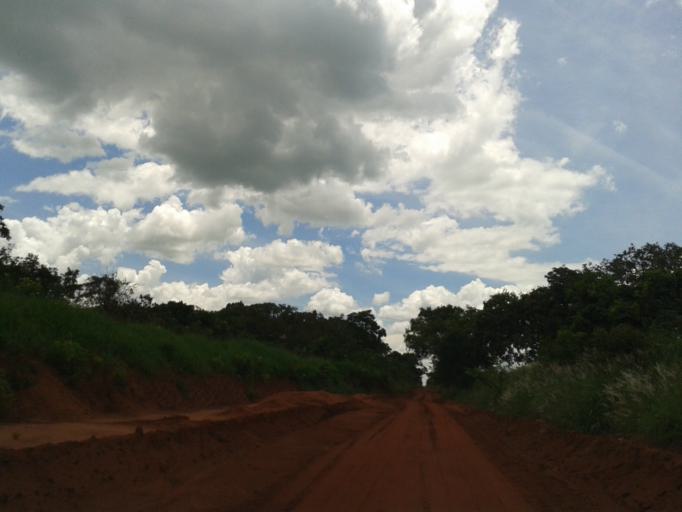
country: BR
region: Minas Gerais
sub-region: Ituiutaba
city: Ituiutaba
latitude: -18.8840
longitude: -49.4725
